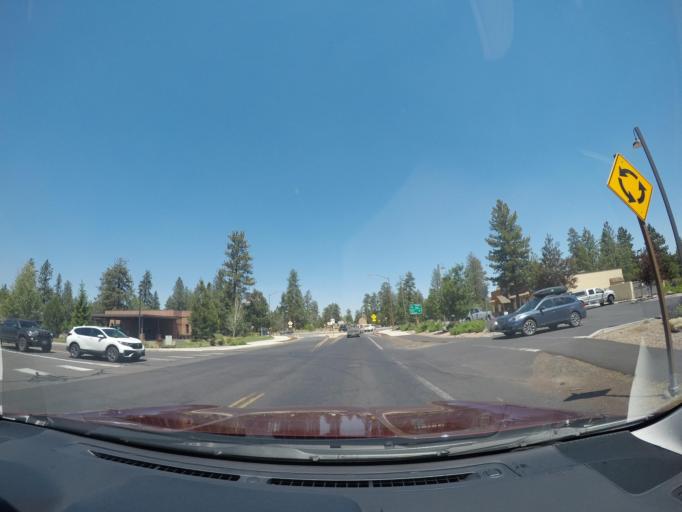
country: US
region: Oregon
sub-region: Deschutes County
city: Sisters
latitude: 44.2952
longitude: -121.5607
